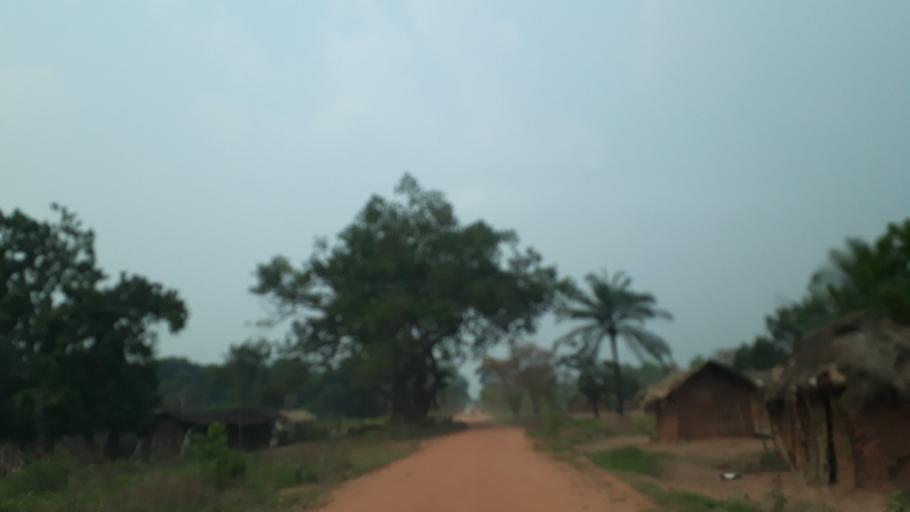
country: CD
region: Kasai-Occidental
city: Tshikapa
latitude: -6.4830
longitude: 20.4302
